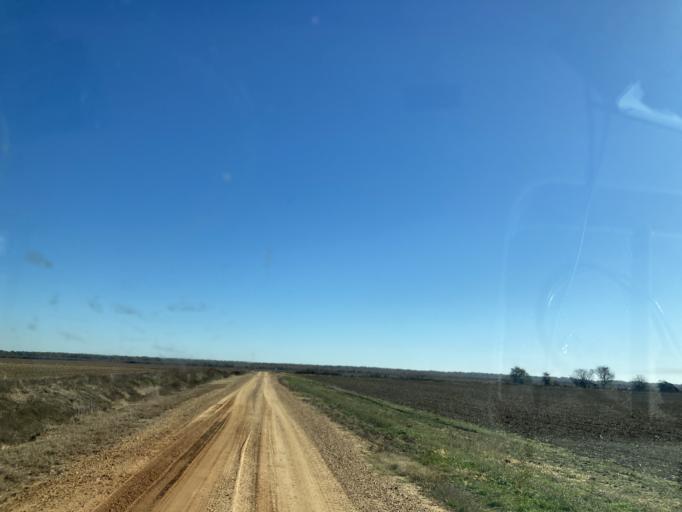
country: US
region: Mississippi
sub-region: Sharkey County
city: Rolling Fork
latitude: 32.8502
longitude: -90.6745
